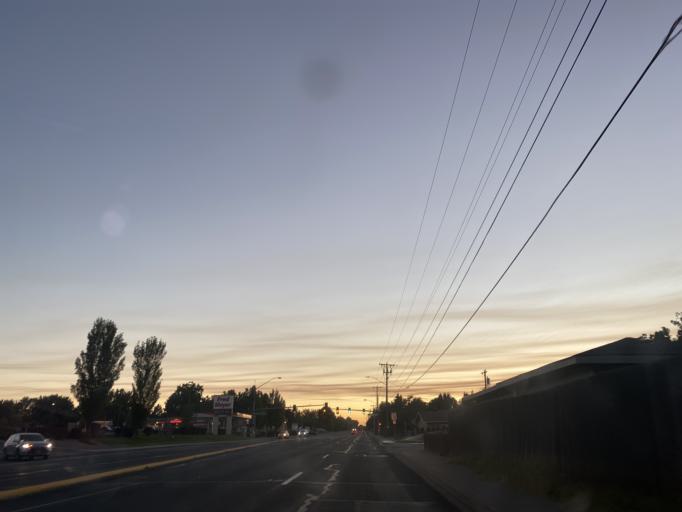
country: US
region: Washington
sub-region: Benton County
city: Kennewick
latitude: 46.1987
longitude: -119.1604
